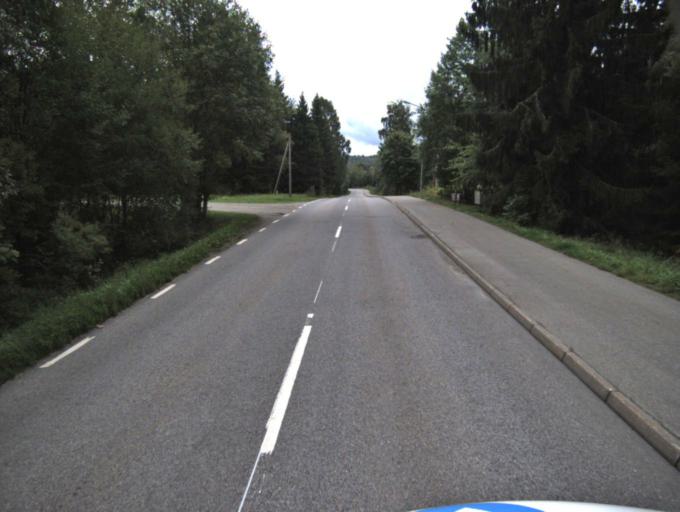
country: SE
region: Vaestra Goetaland
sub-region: Ulricehamns Kommun
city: Ulricehamn
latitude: 57.7710
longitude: 13.4424
